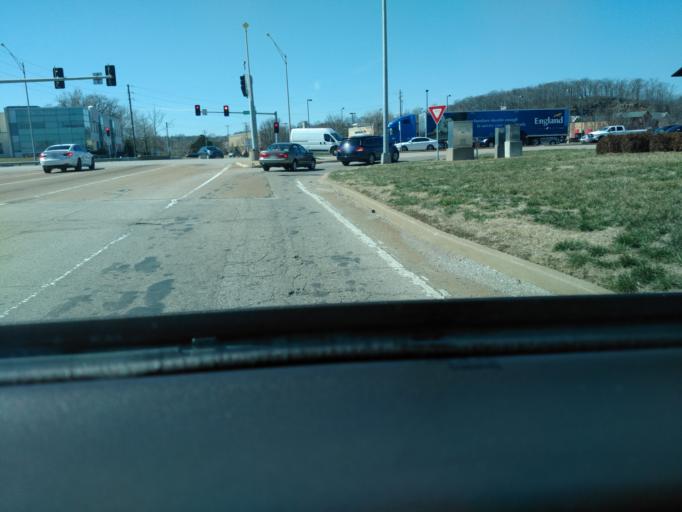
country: US
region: Missouri
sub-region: Saint Louis County
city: Fenton
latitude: 38.5122
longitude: -90.4444
